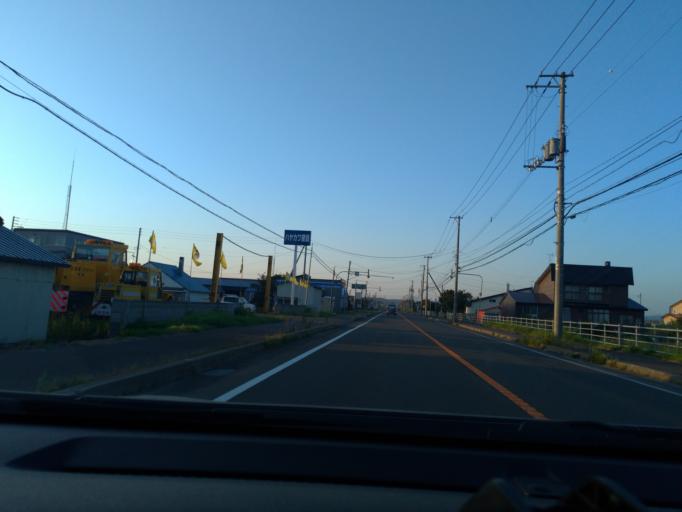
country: JP
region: Hokkaido
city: Tobetsu
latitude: 43.2030
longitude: 141.5210
